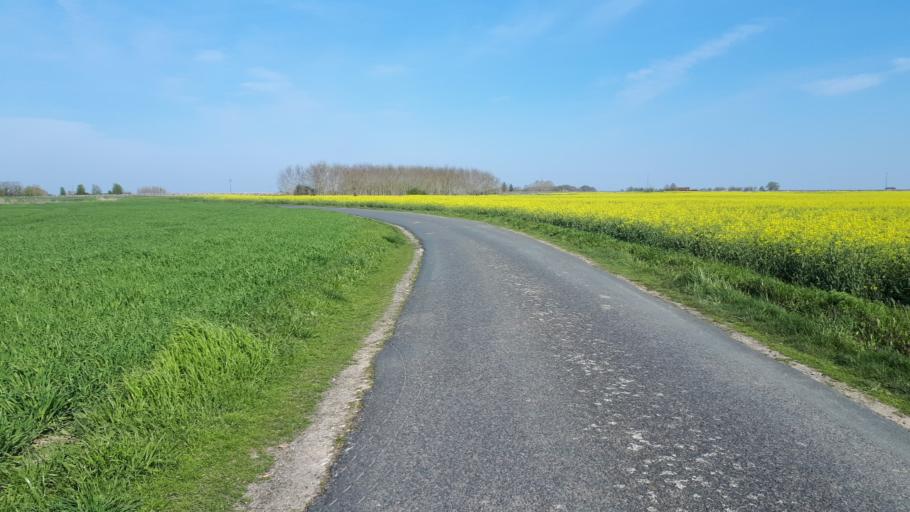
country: FR
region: Centre
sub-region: Departement du Loir-et-Cher
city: Contres
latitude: 47.3843
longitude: 1.3892
